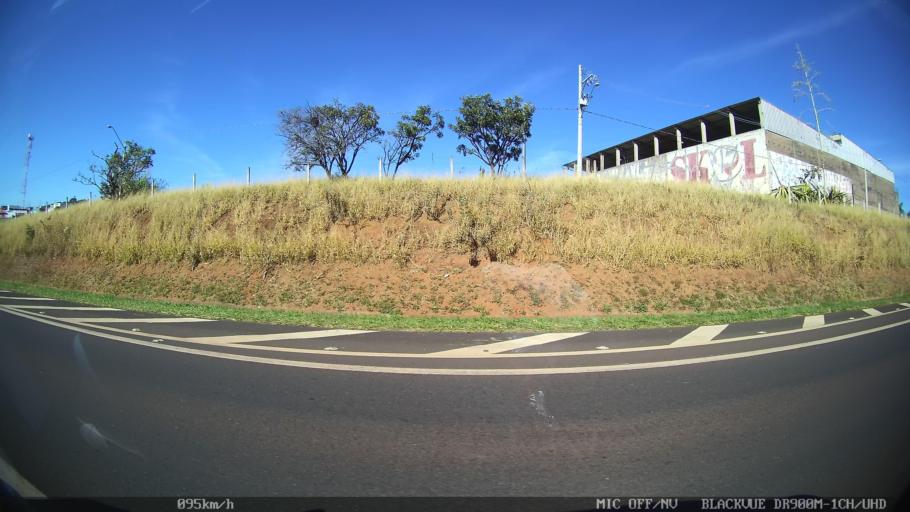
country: BR
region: Sao Paulo
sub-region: Franca
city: Franca
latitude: -20.5718
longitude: -47.3842
